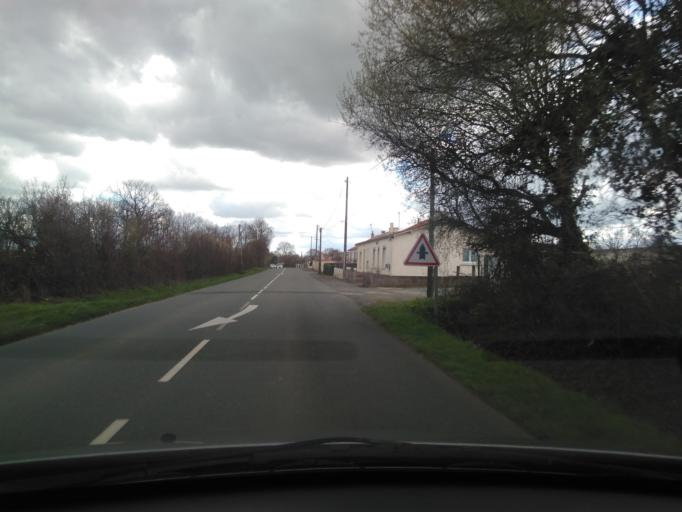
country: FR
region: Pays de la Loire
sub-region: Departement de la Vendee
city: Les Essarts
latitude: 46.7632
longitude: -1.2266
